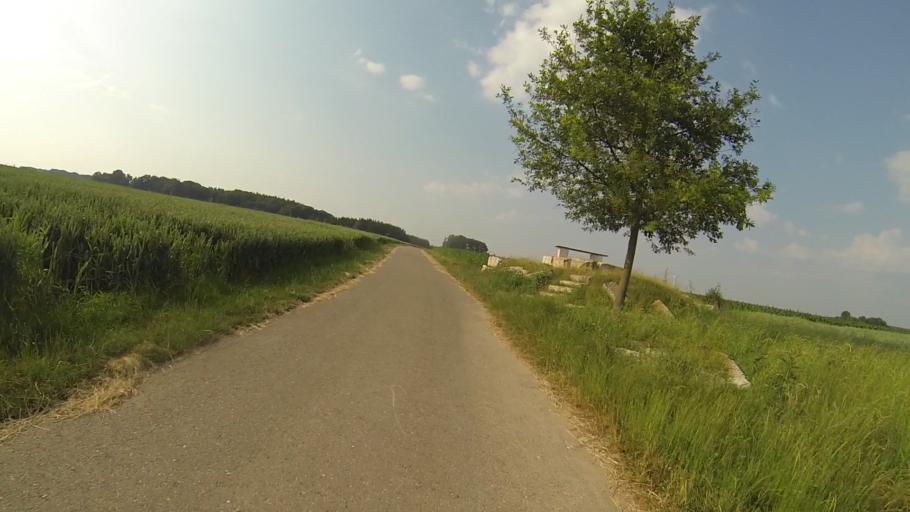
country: DE
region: Bavaria
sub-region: Swabia
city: Neu-Ulm
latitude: 48.4404
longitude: 10.0288
